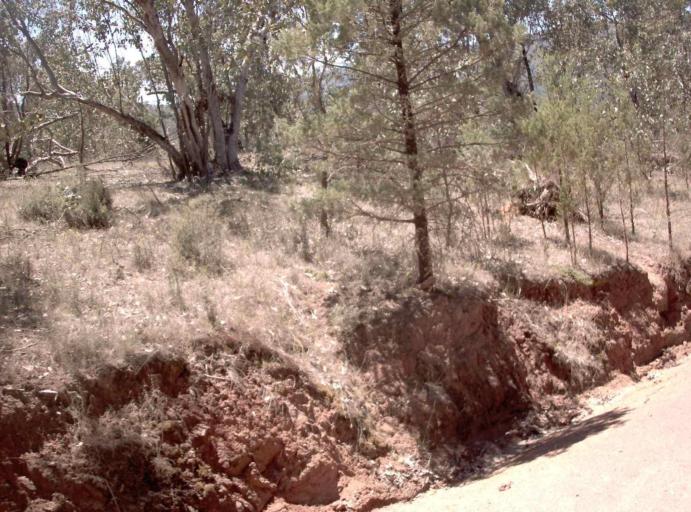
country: AU
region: New South Wales
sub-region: Snowy River
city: Jindabyne
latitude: -36.9267
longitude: 148.3891
